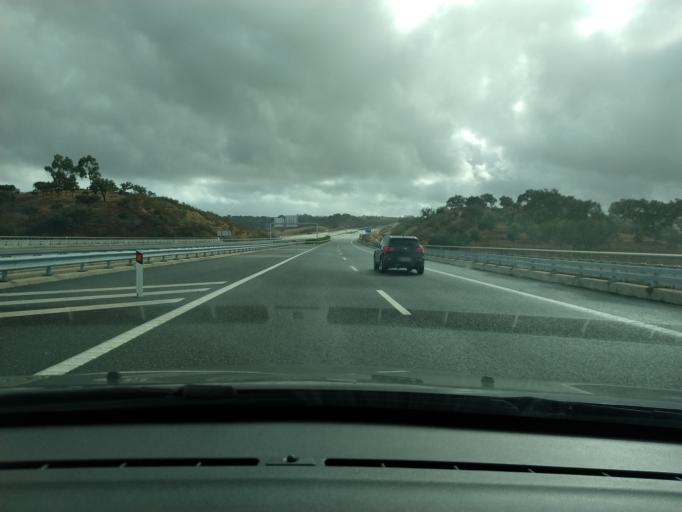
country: PT
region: Beja
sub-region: Almodovar
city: Almodovar
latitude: 37.5165
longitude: -8.1832
